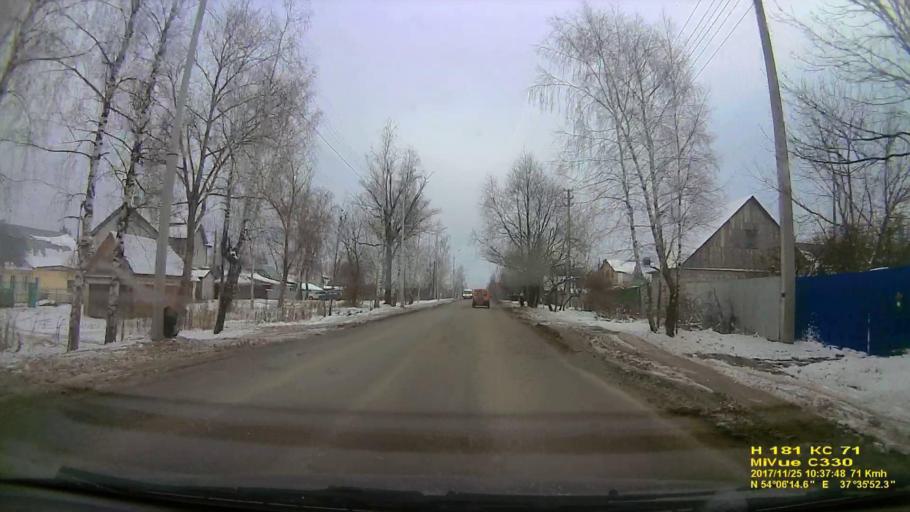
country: RU
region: Tula
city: Skuratovskiy
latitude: 54.1041
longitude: 37.5979
